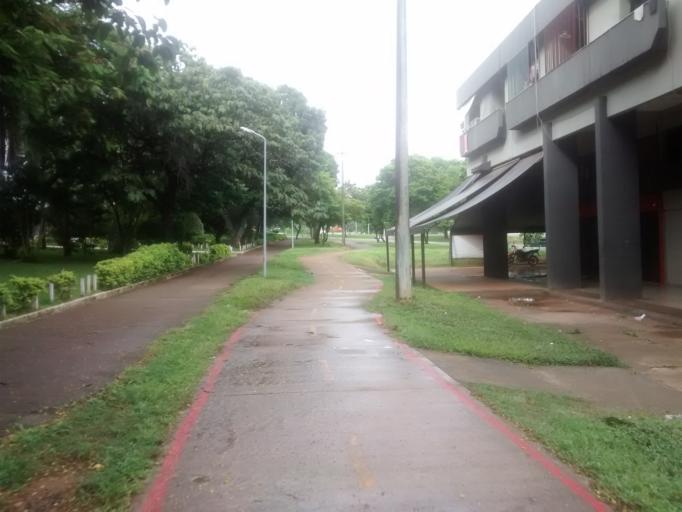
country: BR
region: Federal District
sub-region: Brasilia
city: Brasilia
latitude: -15.7580
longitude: -47.8833
